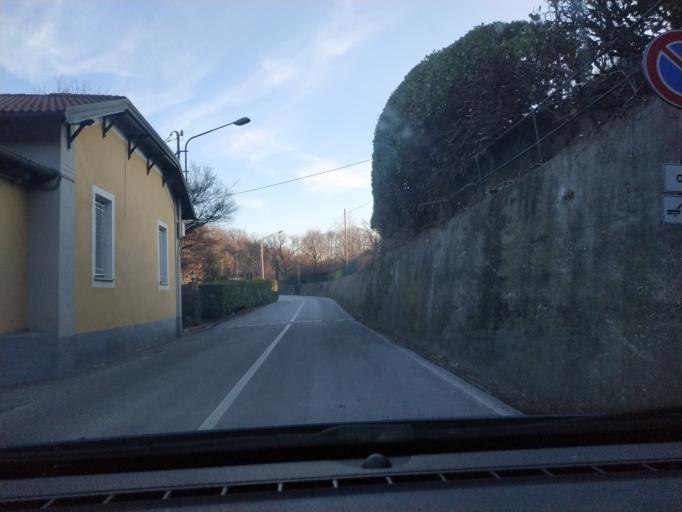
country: IT
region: Piedmont
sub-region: Provincia di Torino
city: Ivrea
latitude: 45.4822
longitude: 7.8788
